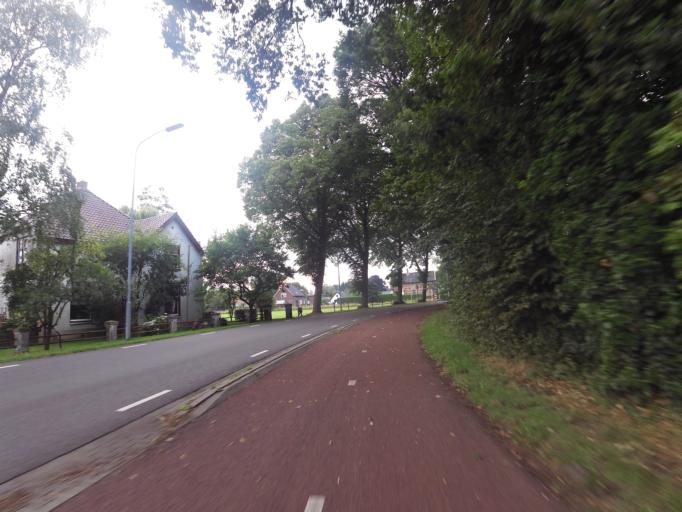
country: NL
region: Gelderland
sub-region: Oude IJsselstreek
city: Gendringen
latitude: 51.8662
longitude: 6.3861
